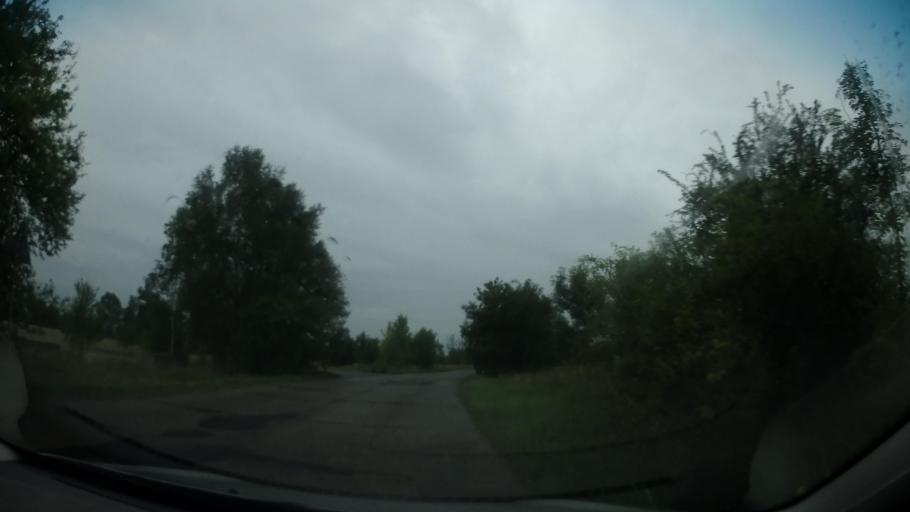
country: CZ
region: Central Bohemia
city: Milovice
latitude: 50.2408
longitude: 14.8976
